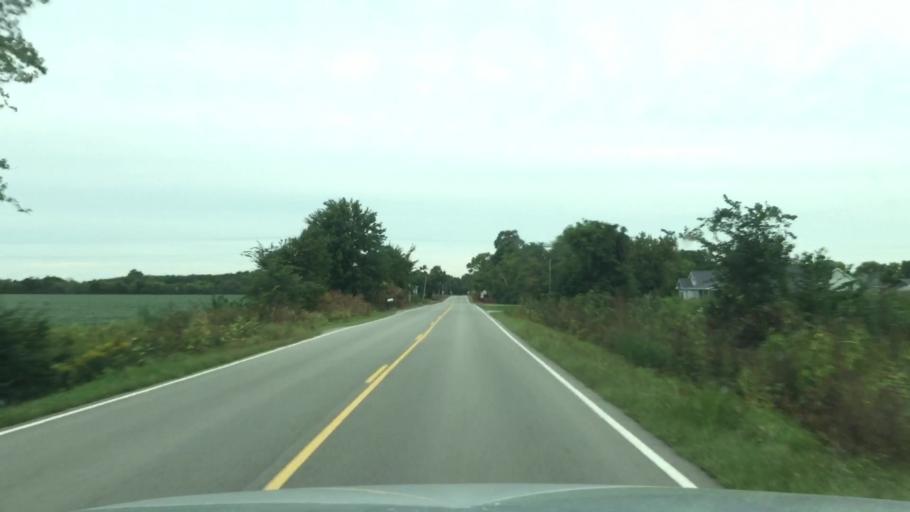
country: US
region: Michigan
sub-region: Washtenaw County
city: Milan
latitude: 42.0890
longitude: -83.7351
